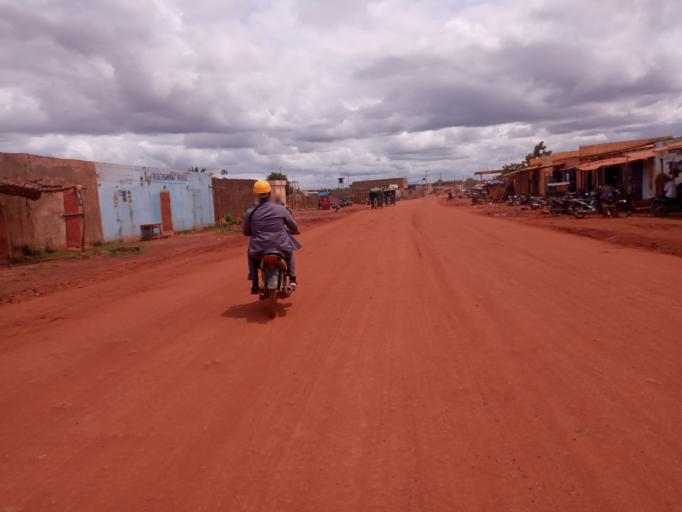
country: ML
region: Bamako
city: Bamako
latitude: 12.5376
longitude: -7.9943
